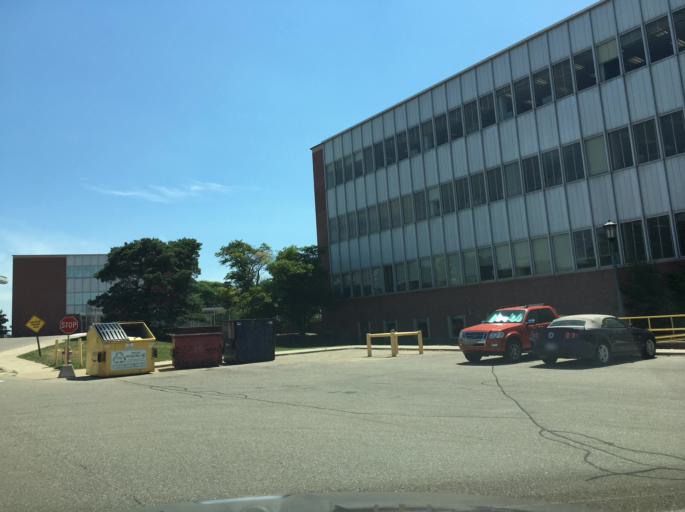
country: US
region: Michigan
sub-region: Wayne County
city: Allen Park
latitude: 42.2938
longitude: -83.2303
